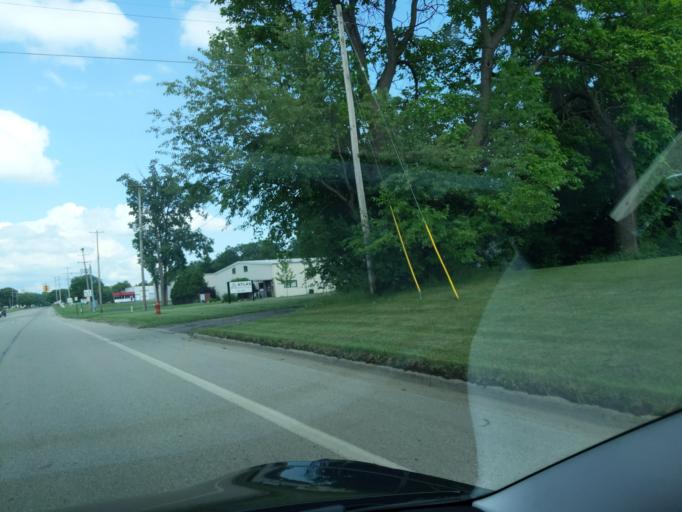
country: US
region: Michigan
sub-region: Jackson County
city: Jackson
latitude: 42.2332
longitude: -84.3858
